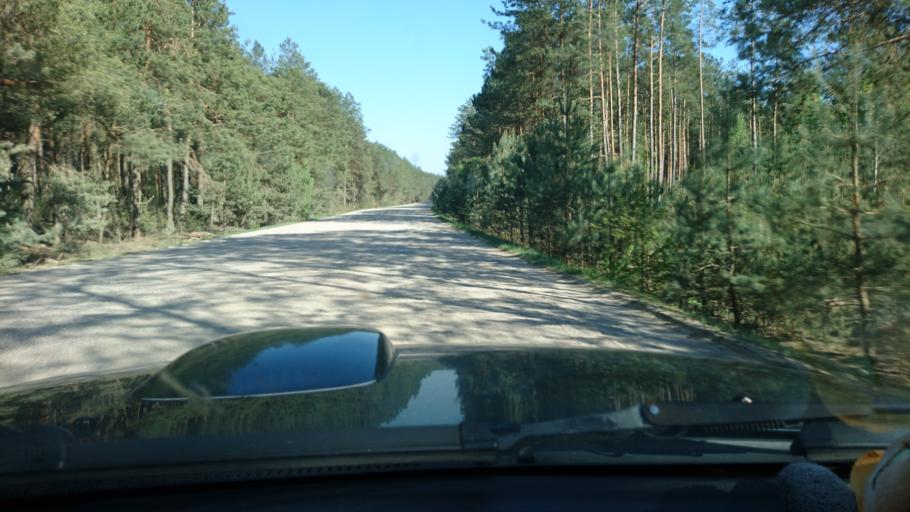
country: BY
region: Brest
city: Zhabinka
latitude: 52.3873
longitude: 24.1062
